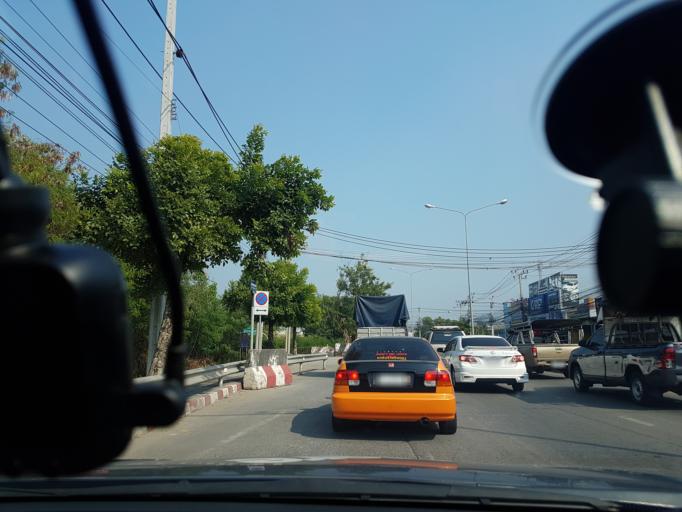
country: TH
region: Bangkok
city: Khlong Sam Wa
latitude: 13.8619
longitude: 100.7212
